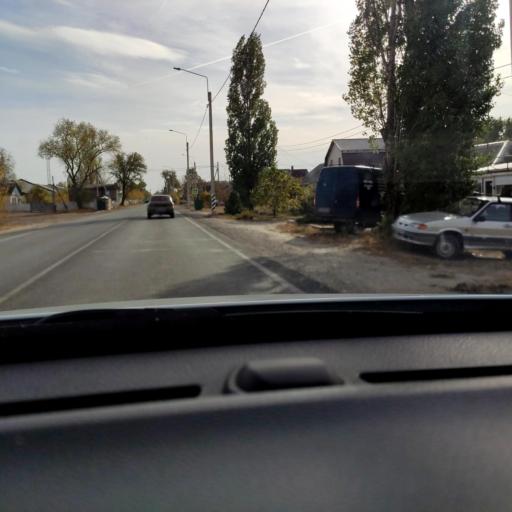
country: RU
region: Voronezj
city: Maslovka
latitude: 51.5675
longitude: 39.2459
